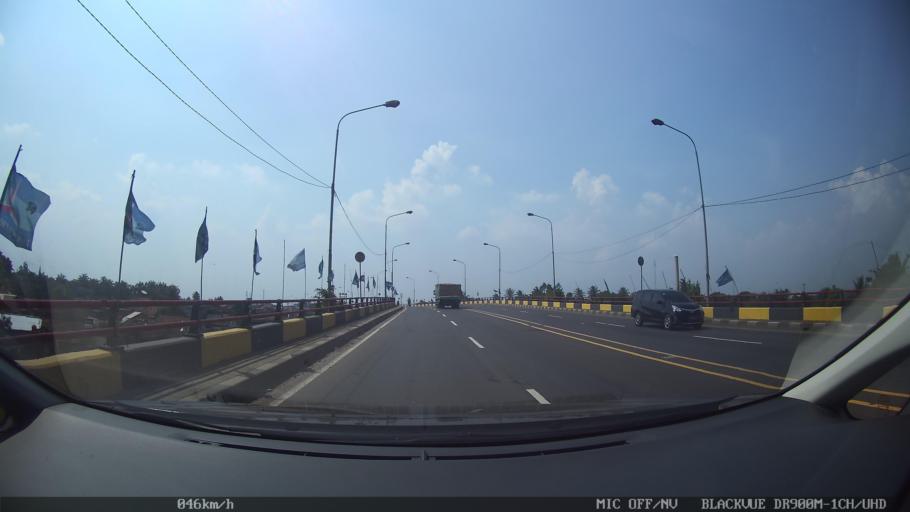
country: ID
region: Lampung
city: Natar
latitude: -5.3217
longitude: 105.2000
